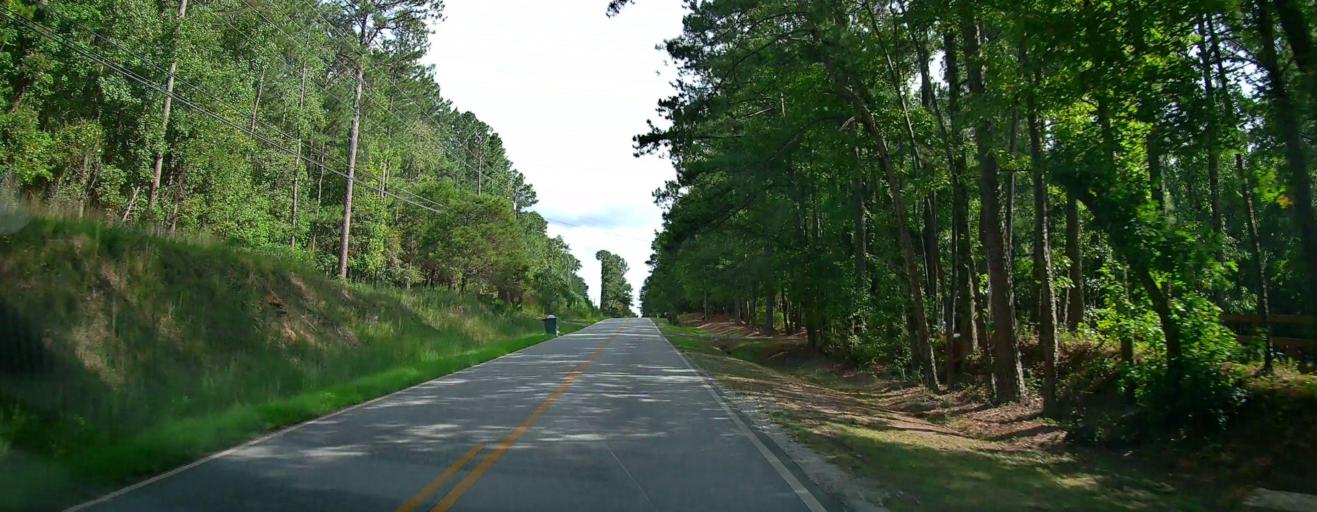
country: US
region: Alabama
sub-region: Russell County
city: Phenix City
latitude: 32.6013
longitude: -84.9806
